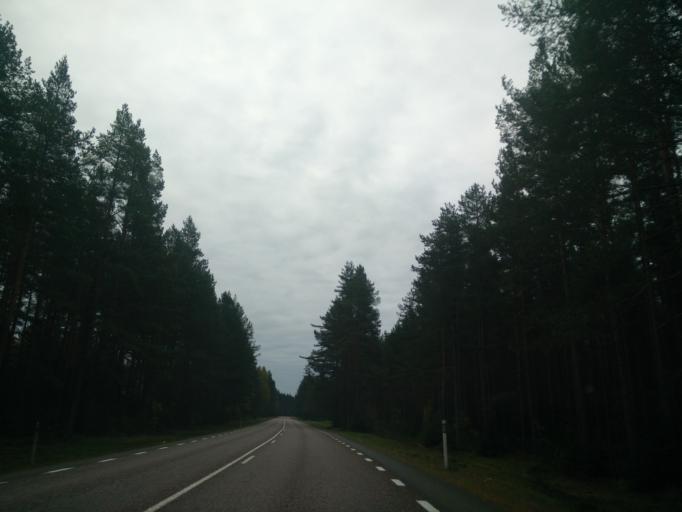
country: SE
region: Gaevleborg
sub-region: Gavle Kommun
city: Norrsundet
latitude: 60.8641
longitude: 17.1739
